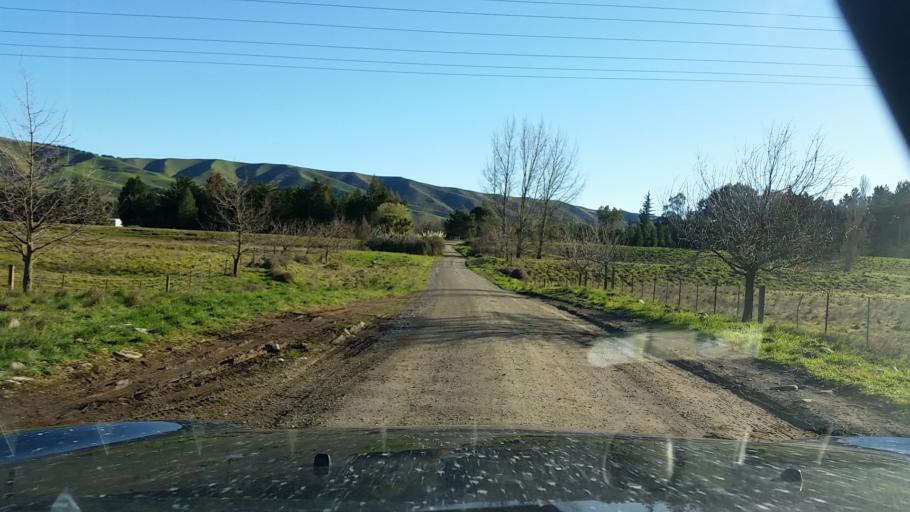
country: NZ
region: Marlborough
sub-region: Marlborough District
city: Blenheim
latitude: -41.6219
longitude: 173.6850
